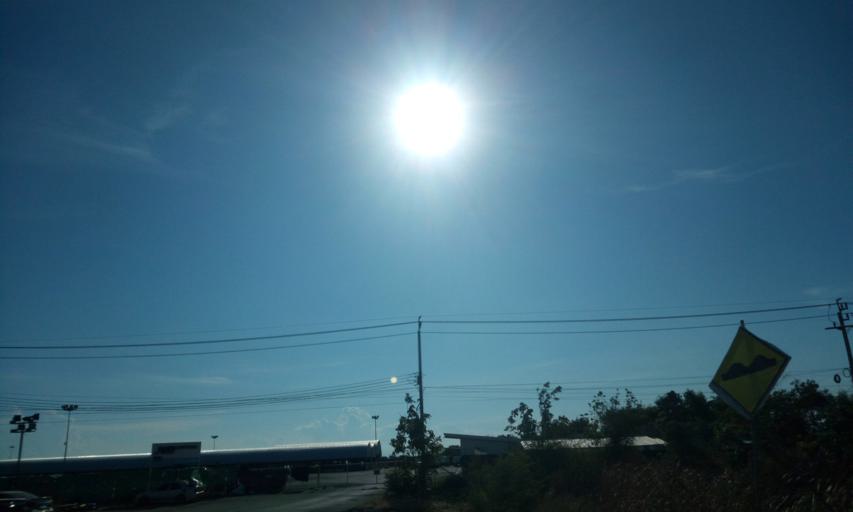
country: TH
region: Samut Prakan
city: Bang Bo District
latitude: 13.5390
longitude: 100.7503
